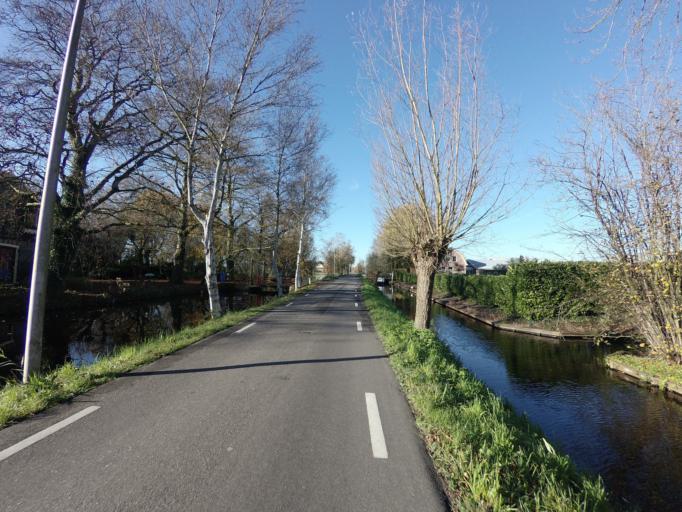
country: NL
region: South Holland
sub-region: Gemeente Nieuwkoop
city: Nieuwkoop
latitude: 52.1316
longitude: 4.7470
